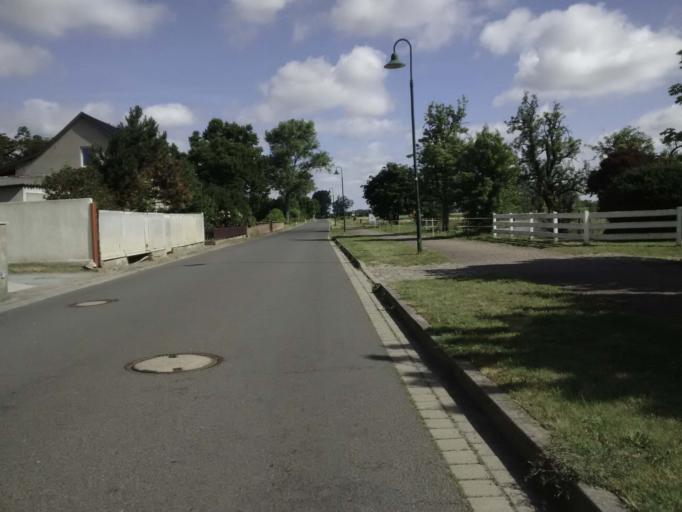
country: DE
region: Saxony-Anhalt
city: Jerichow
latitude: 52.4181
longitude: 11.9645
